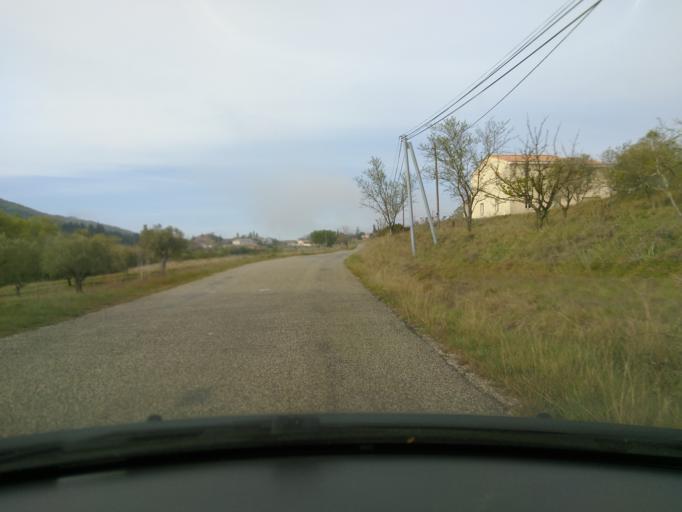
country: FR
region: Rhone-Alpes
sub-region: Departement de l'Ardeche
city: Ruoms
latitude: 44.4564
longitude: 4.4017
